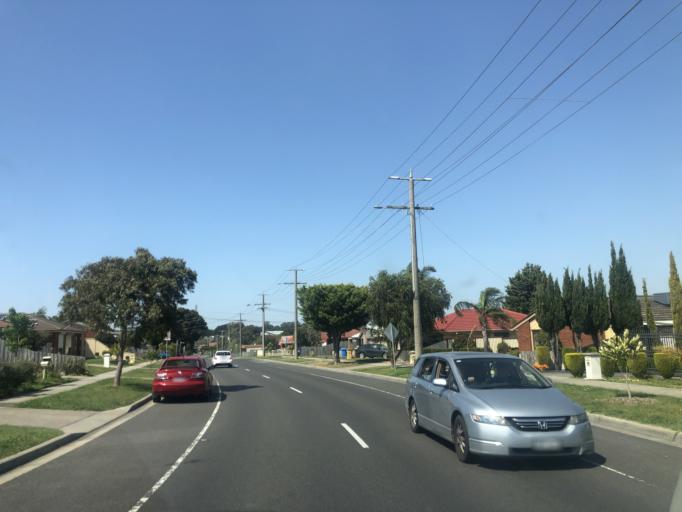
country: AU
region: Victoria
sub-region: Casey
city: Hallam
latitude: -38.0325
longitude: 145.2760
